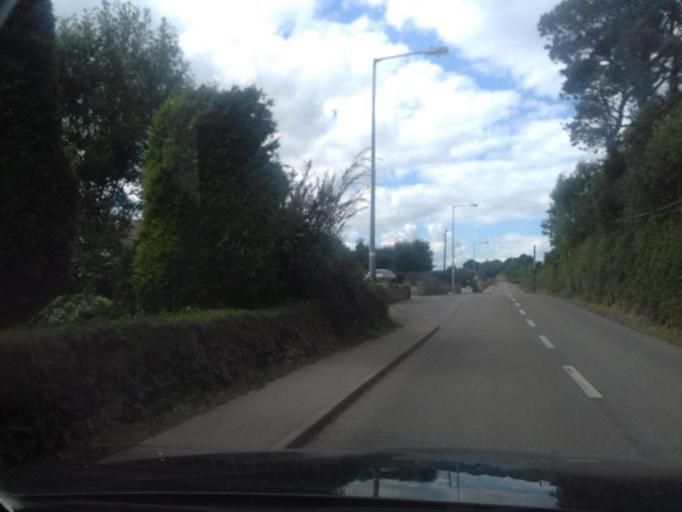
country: IE
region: Munster
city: Carrick-on-Suir
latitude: 52.2808
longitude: -7.4425
